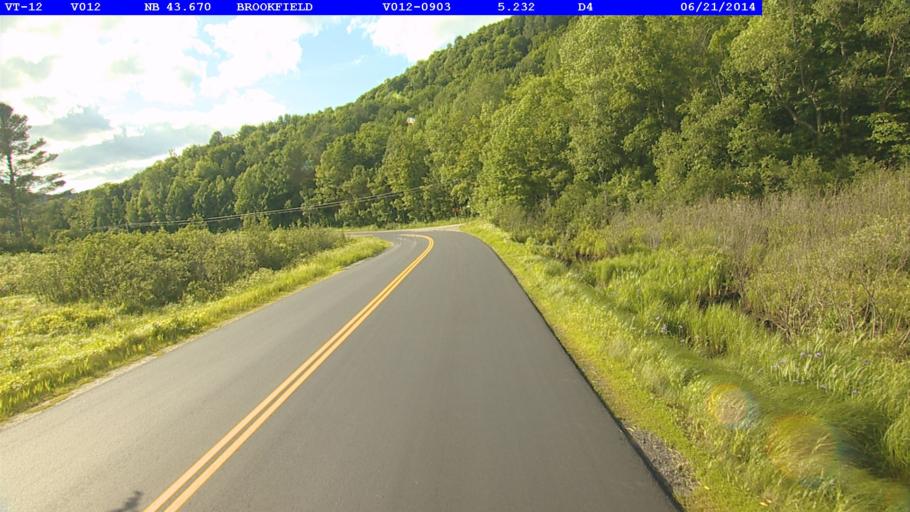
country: US
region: Vermont
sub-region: Washington County
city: Northfield
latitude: 44.0746
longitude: -72.6378
